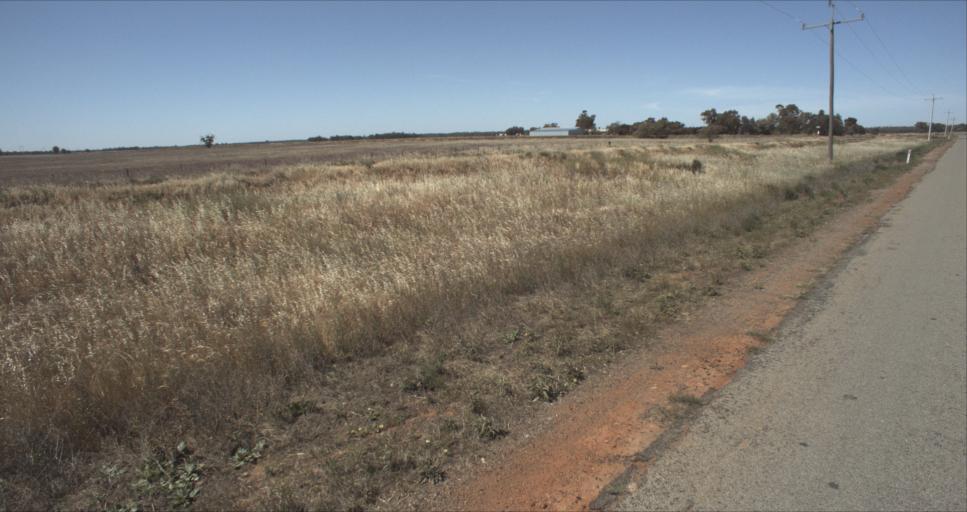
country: AU
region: New South Wales
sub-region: Leeton
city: Leeton
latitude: -34.5797
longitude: 146.3090
